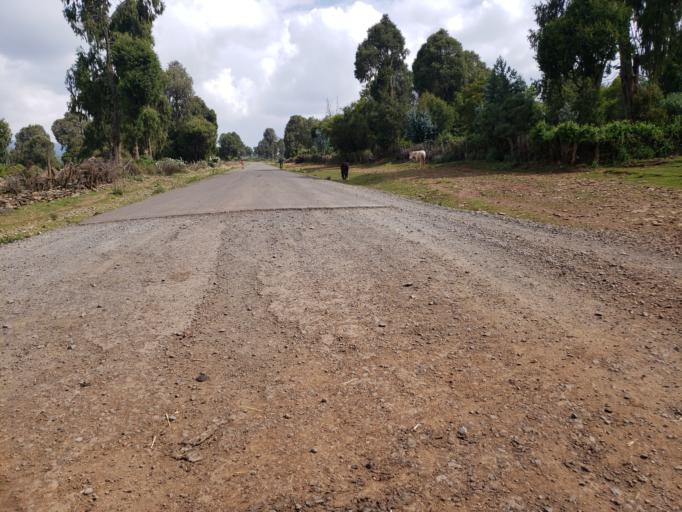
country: ET
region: Oromiya
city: Dodola
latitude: 6.8667
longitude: 39.3900
